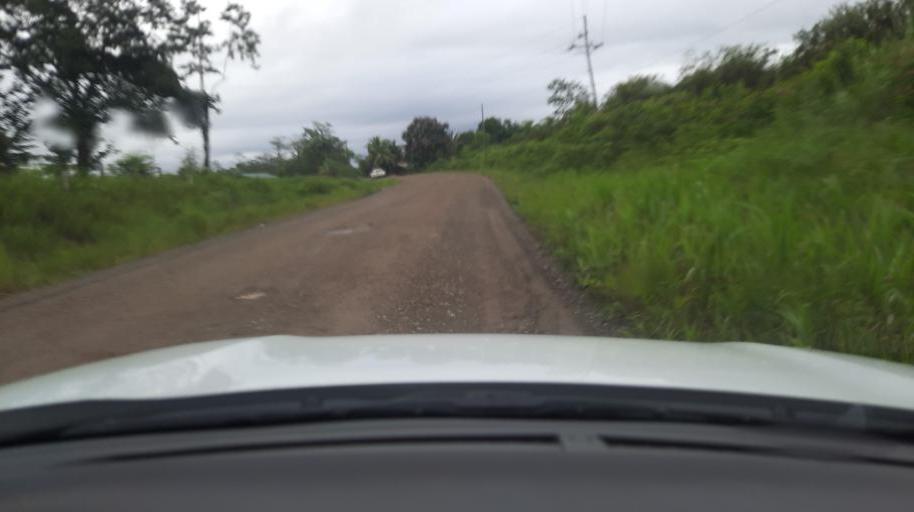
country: CR
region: Alajuela
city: San Jose
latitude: 10.9924
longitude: -85.2763
